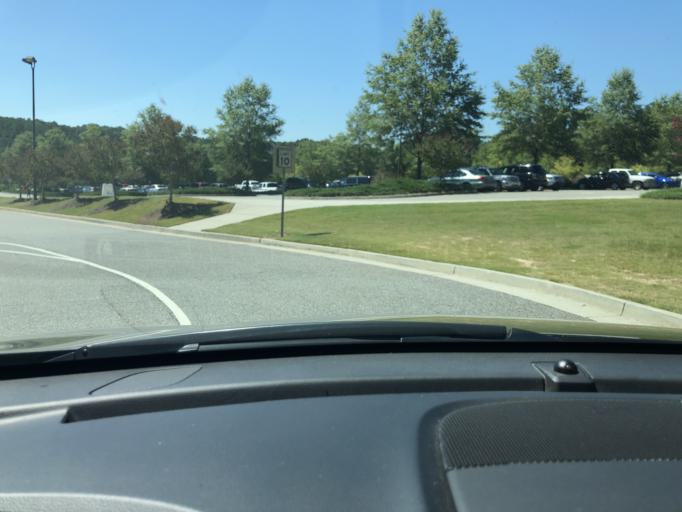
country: US
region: Georgia
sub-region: Gwinnett County
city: Grayson
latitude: 33.9170
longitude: -83.8951
